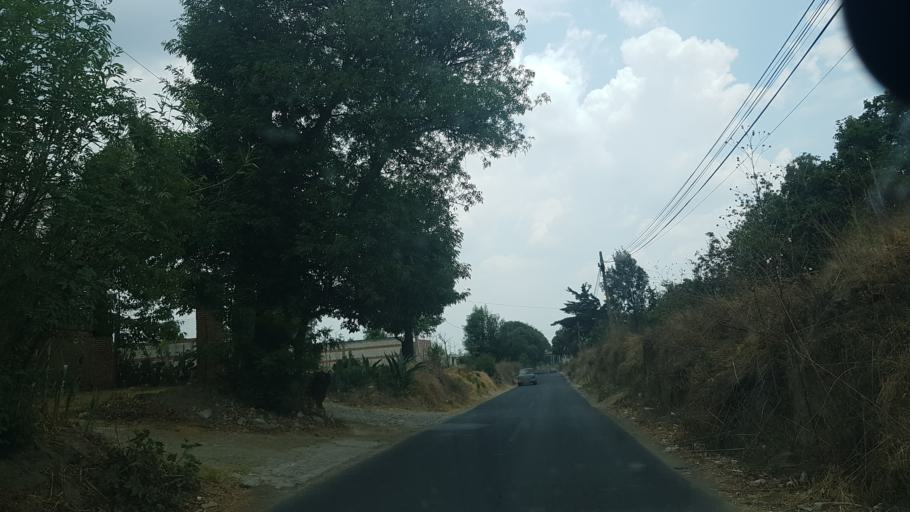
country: MX
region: Puebla
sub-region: Huejotzingo
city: San Miguel Tianguizolco
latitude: 19.1592
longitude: -98.4279
